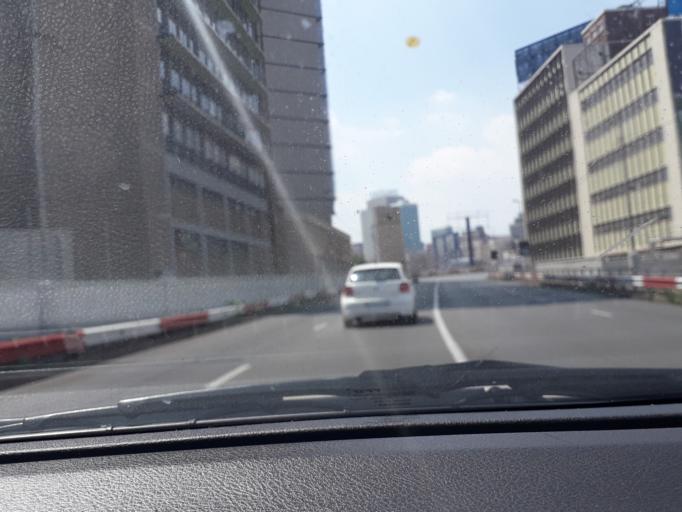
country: ZA
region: Gauteng
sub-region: City of Johannesburg Metropolitan Municipality
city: Johannesburg
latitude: -26.1960
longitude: 28.0358
